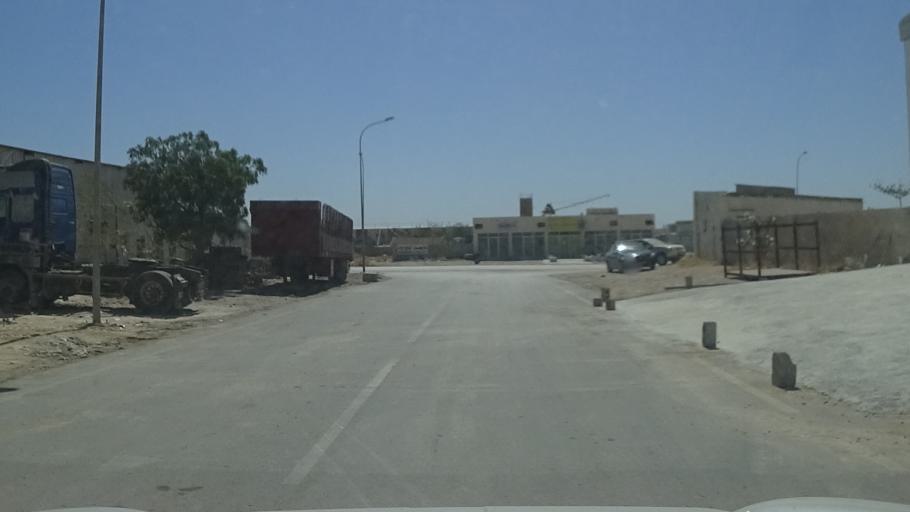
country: OM
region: Zufar
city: Salalah
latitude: 17.0338
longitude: 54.0414
